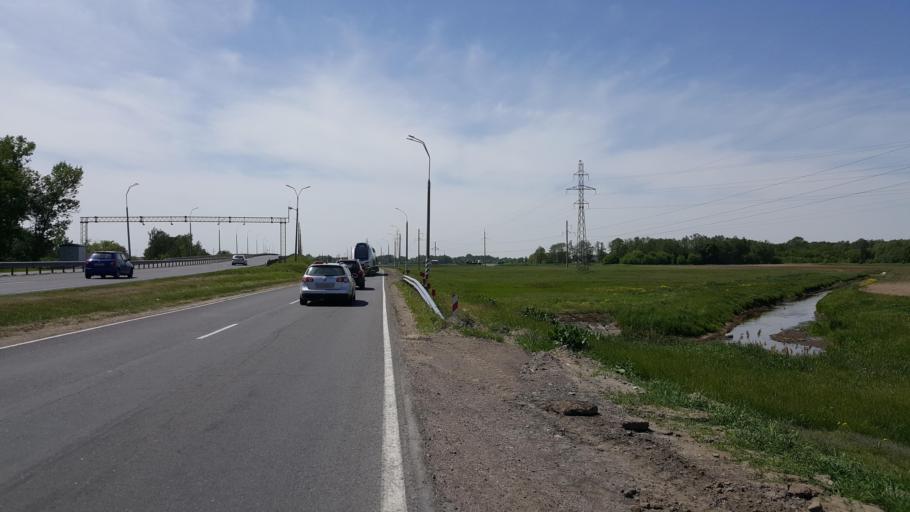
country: BY
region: Brest
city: Brest
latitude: 52.1512
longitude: 23.6861
